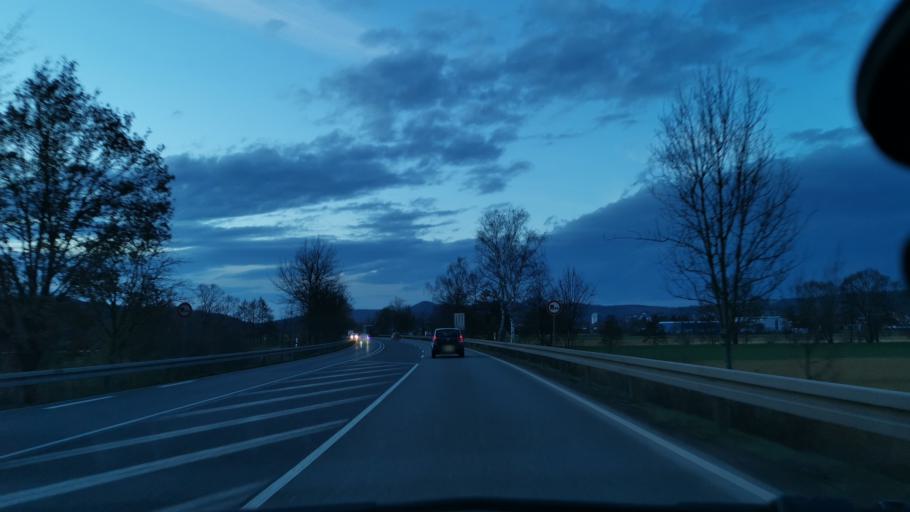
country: DE
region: Hesse
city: Breitenbach
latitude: 50.9625
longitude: 9.7889
